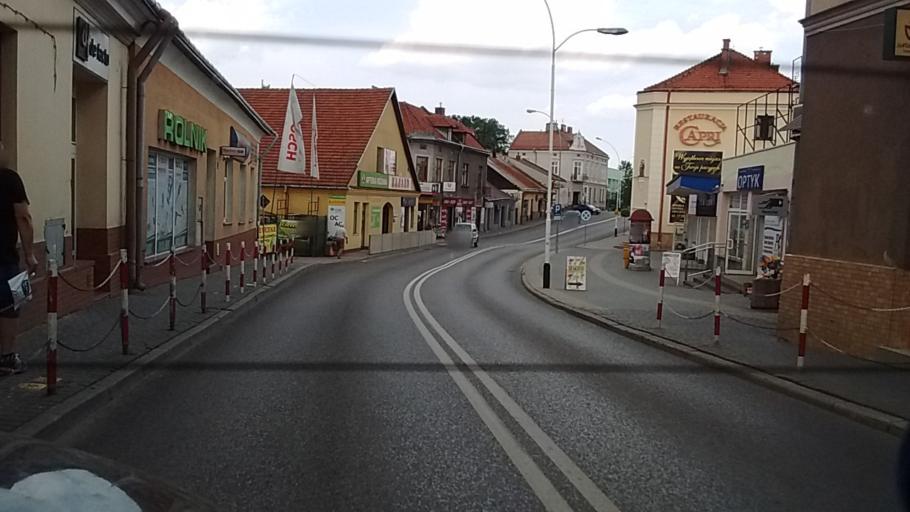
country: PL
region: Subcarpathian Voivodeship
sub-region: Powiat lezajski
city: Lezajsk
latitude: 50.2538
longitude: 22.4222
